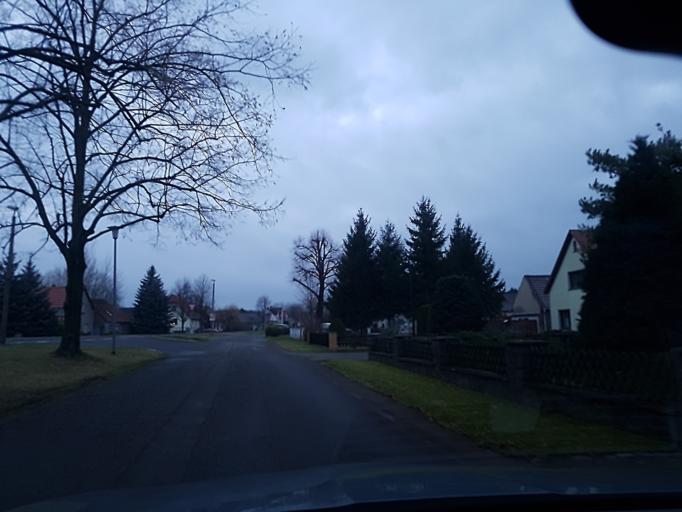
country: DE
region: Brandenburg
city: Schonborn
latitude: 51.5964
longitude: 13.4990
